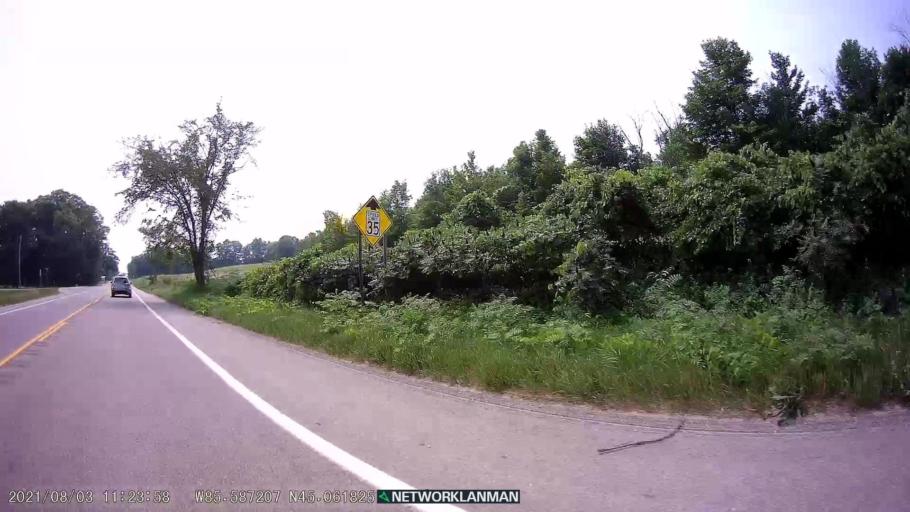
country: US
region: Michigan
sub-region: Leelanau County
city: Leland
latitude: 45.0618
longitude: -85.5872
